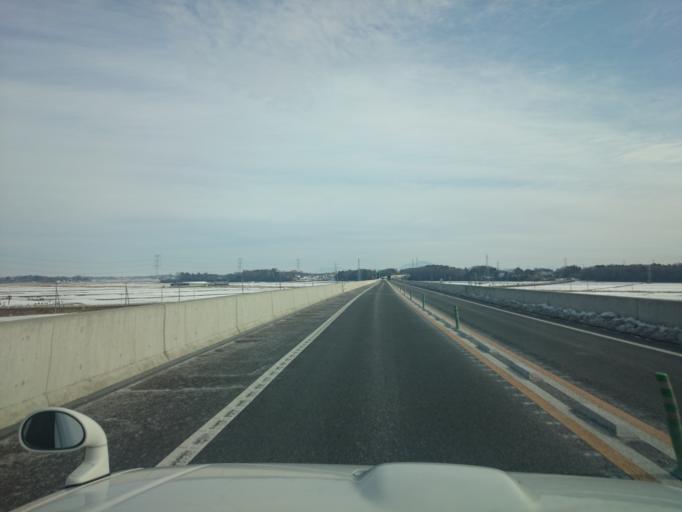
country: JP
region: Ibaraki
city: Sakai
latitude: 36.1242
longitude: 139.7803
